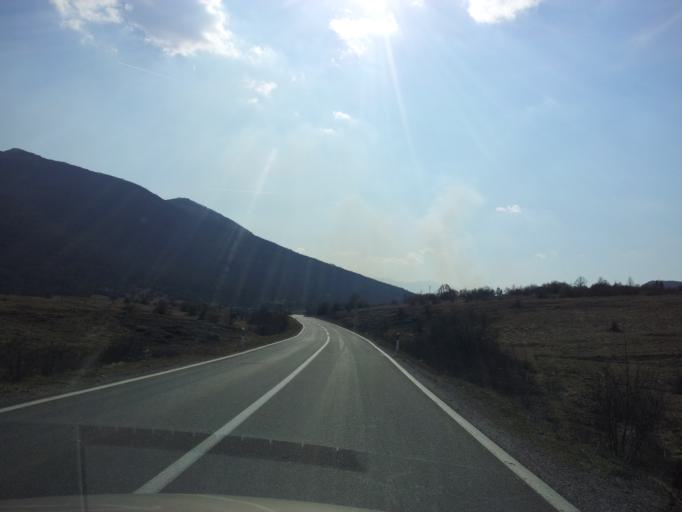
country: HR
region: Zadarska
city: Gracac
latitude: 44.4725
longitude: 15.7206
